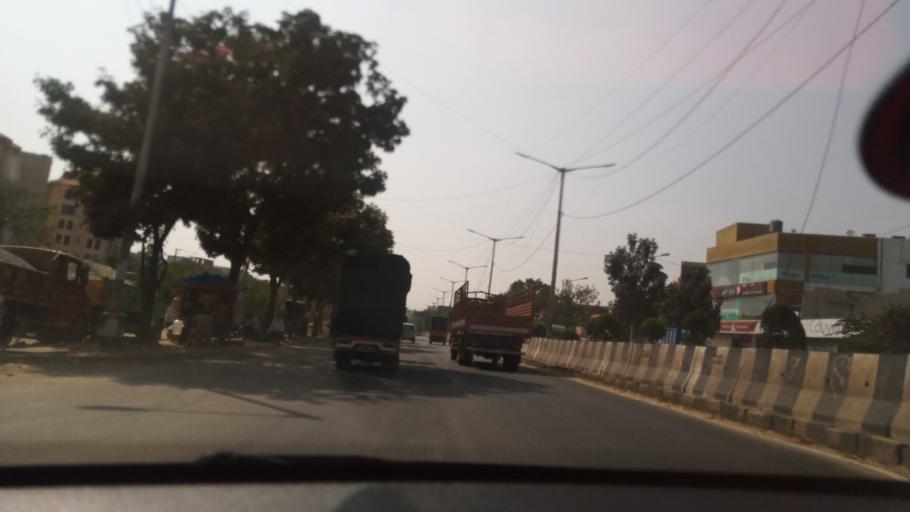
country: IN
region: Karnataka
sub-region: Bangalore Urban
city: Yelahanka
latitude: 13.0472
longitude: 77.5733
